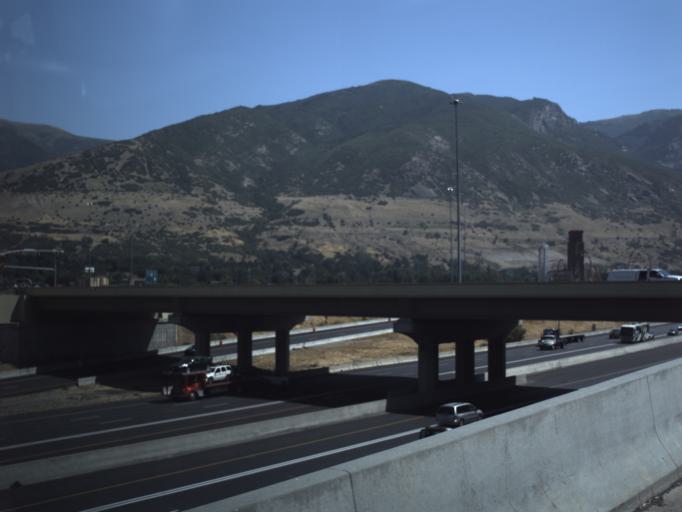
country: US
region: Utah
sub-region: Davis County
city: Farmington
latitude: 40.9896
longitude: -111.9069
